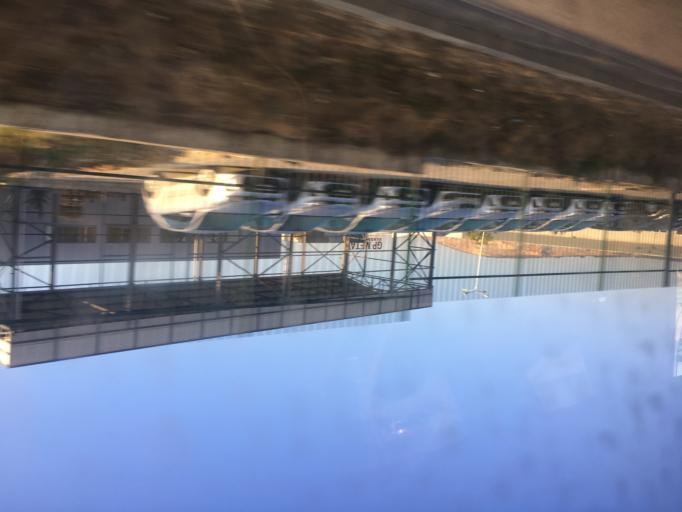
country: XK
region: Pristina
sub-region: Komuna e Drenasit
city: Glogovac
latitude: 42.6014
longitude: 20.9594
